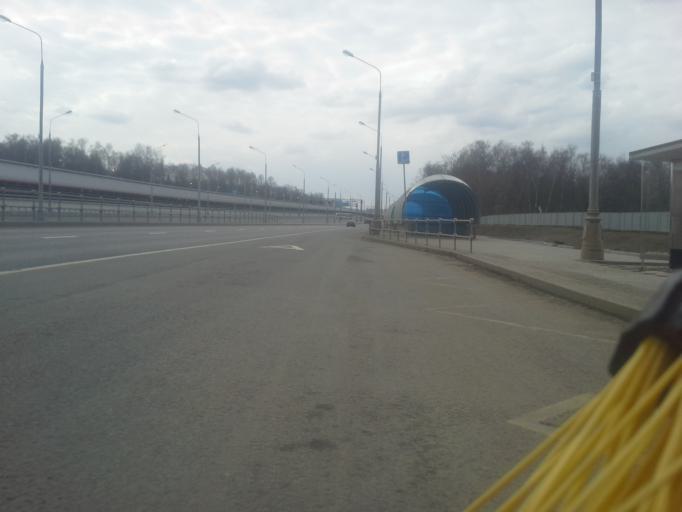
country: RU
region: Moskovskaya
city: Mosrentgen
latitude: 55.5903
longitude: 37.4253
